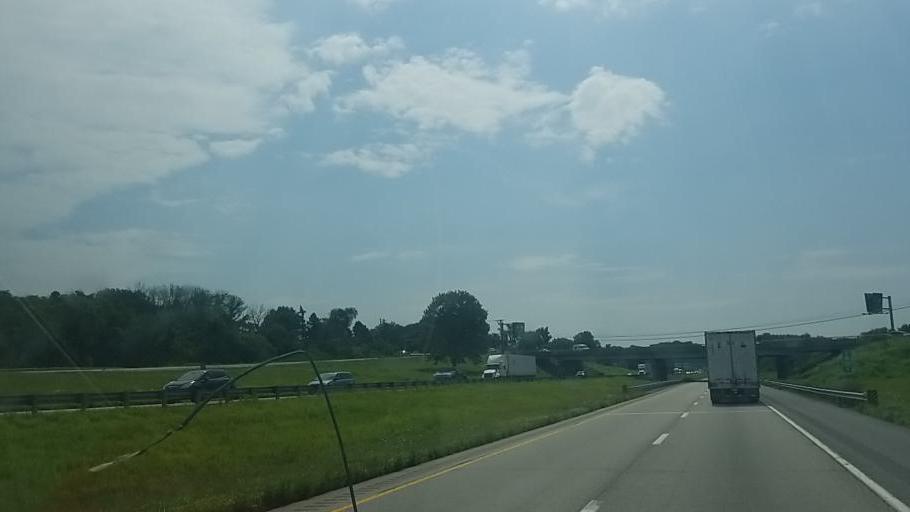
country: US
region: Pennsylvania
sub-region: Perry County
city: Marysville
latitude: 40.3272
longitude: -76.8926
